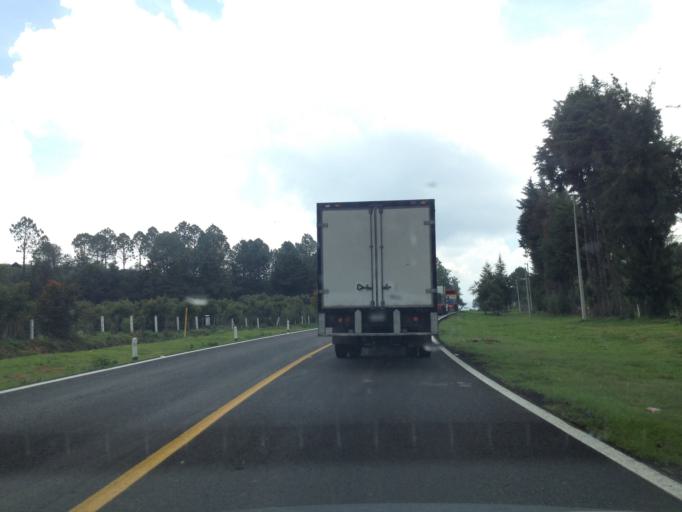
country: MX
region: Michoacan
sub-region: Patzcuaro
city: Santa Maria Huiramangaro (San Juan Tumbio)
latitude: 19.4933
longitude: -101.7485
